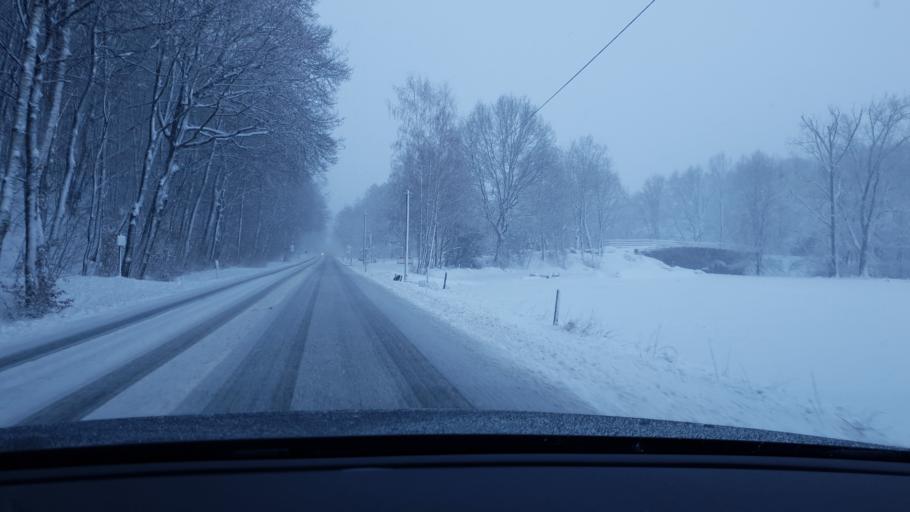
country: DE
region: Saxony
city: Claussnitz
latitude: 50.9117
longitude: 12.8993
